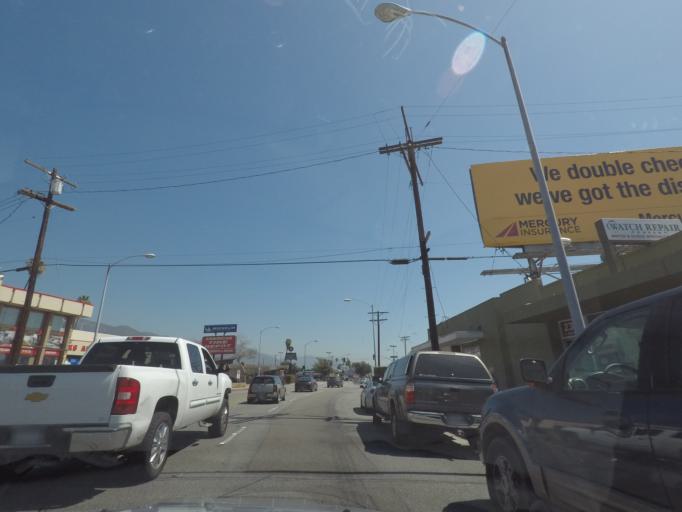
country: US
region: California
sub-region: Los Angeles County
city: East Pasadena
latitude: 34.1497
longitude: -118.1013
